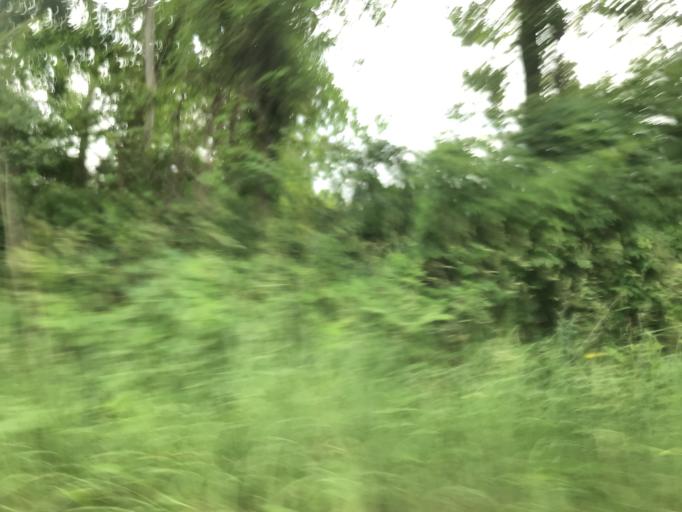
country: US
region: Michigan
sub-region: Oakland County
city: South Lyon
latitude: 42.4472
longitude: -83.6225
